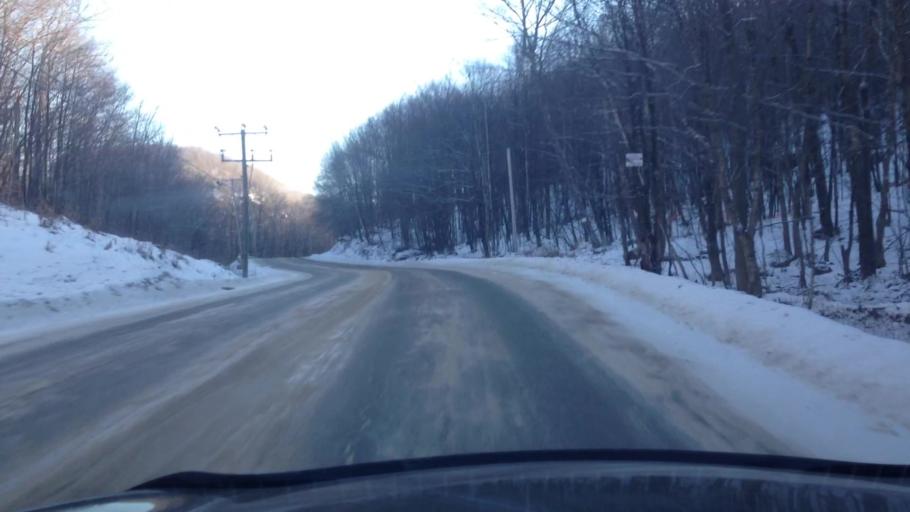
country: CA
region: Quebec
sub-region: Laurentides
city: Brownsburg-Chatham
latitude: 45.9228
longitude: -74.5144
